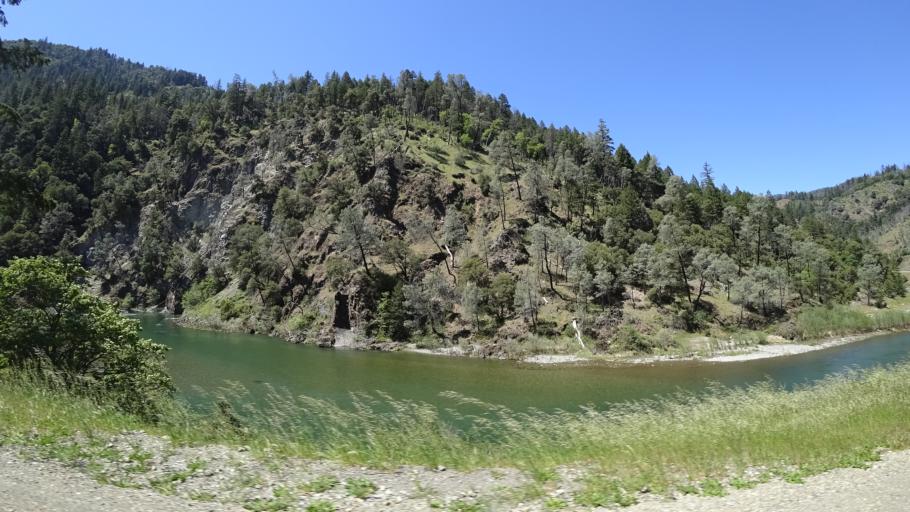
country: US
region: California
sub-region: Trinity County
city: Hayfork
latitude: 40.7854
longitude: -123.3490
